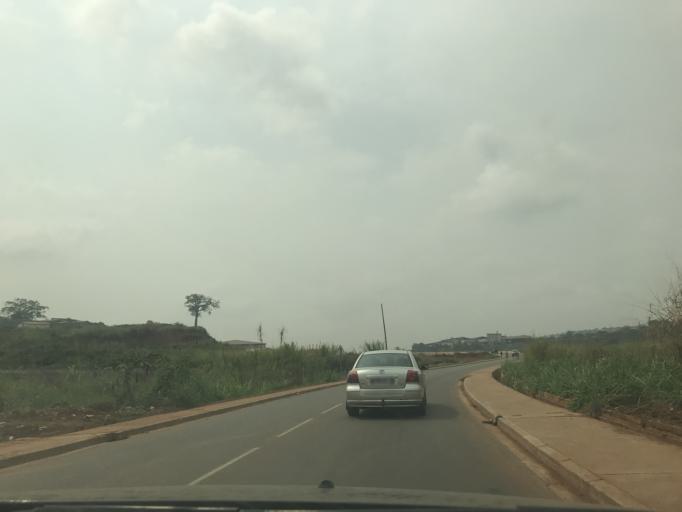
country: CM
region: Centre
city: Yaounde
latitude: 3.8265
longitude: 11.5134
